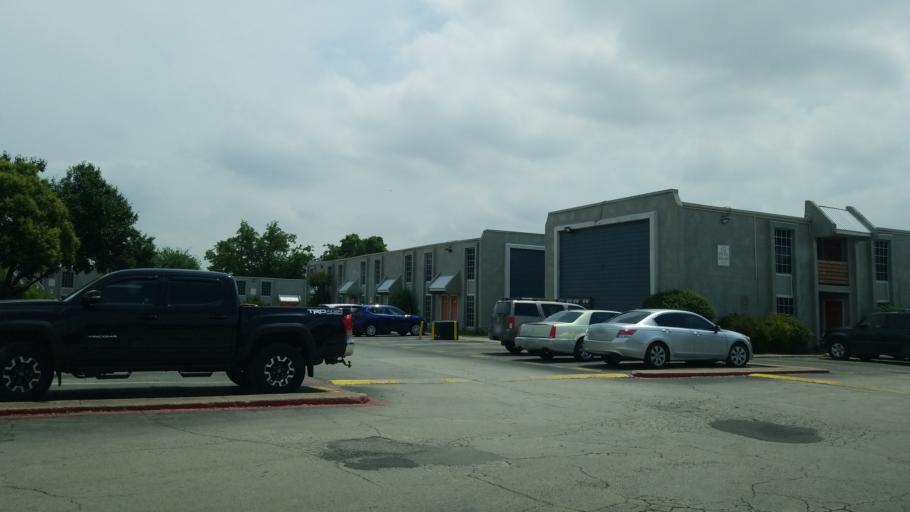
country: US
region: Texas
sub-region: Dallas County
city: Farmers Branch
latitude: 32.9075
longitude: -96.8813
